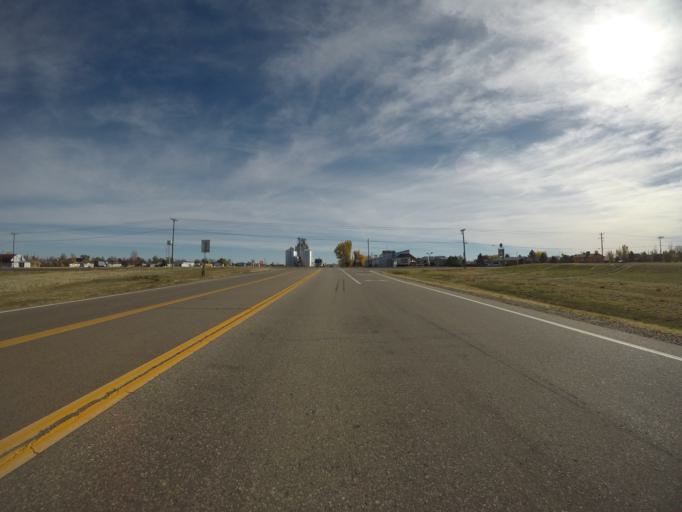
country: US
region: Colorado
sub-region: Adams County
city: Bennett
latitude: 39.7559
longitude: -104.4342
